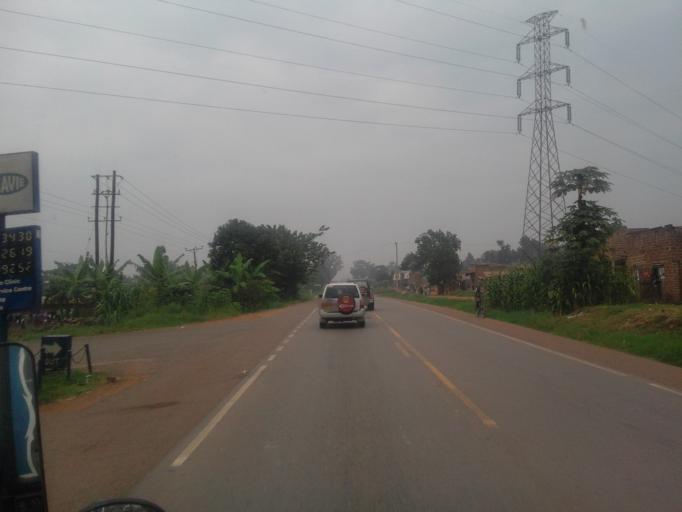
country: UG
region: Central Region
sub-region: Mukono District
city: Mukono
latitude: 0.3807
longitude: 32.8337
